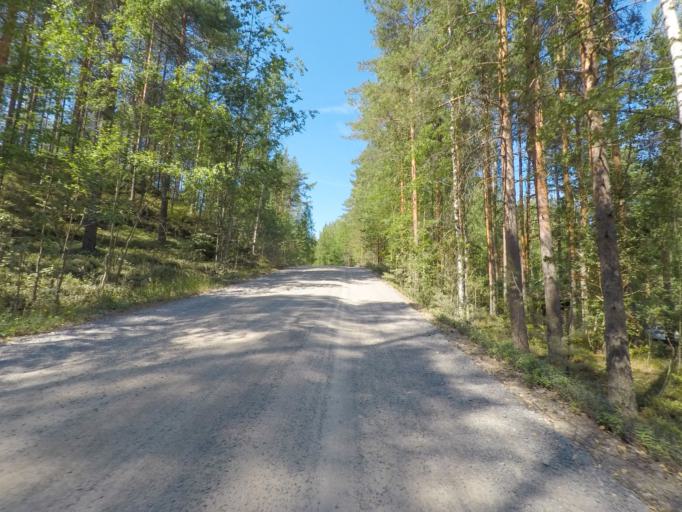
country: FI
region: Southern Savonia
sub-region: Mikkeli
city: Puumala
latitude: 61.4222
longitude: 28.0415
